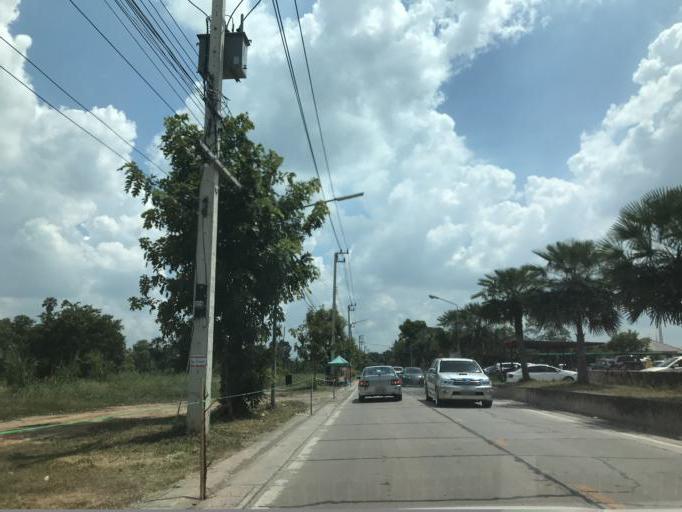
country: TH
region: Phra Nakhon Si Ayutthaya
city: Ban Bang Kadi Pathum Thani
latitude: 14.0068
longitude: 100.5421
